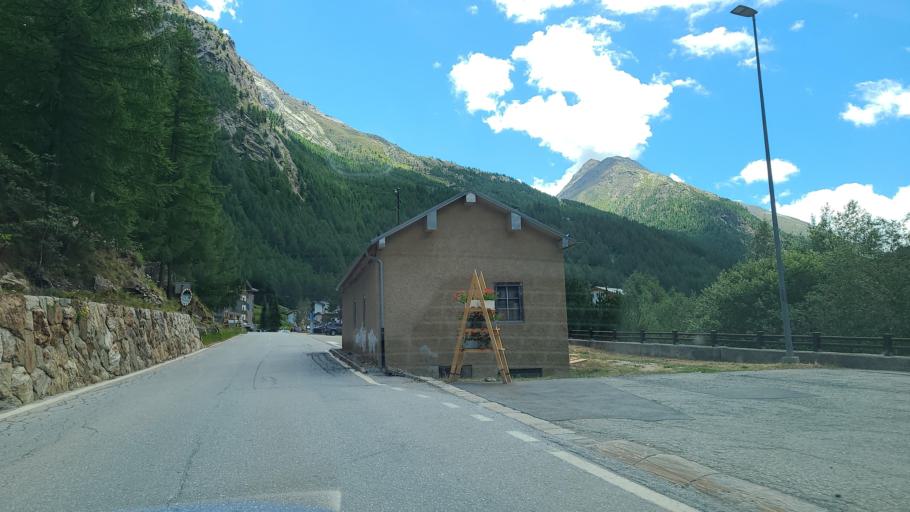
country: CH
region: Valais
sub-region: Visp District
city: Saas-Fee
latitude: 46.0990
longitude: 7.9546
